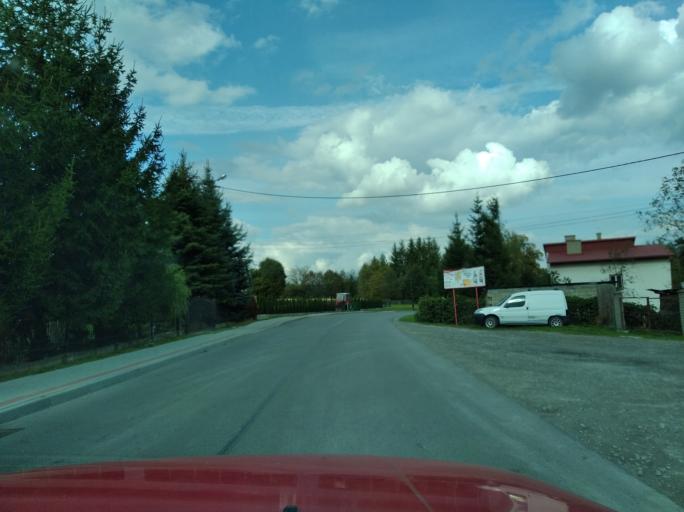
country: PL
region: Subcarpathian Voivodeship
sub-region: Powiat rzeszowski
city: Tyczyn
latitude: 49.9530
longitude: 22.0277
